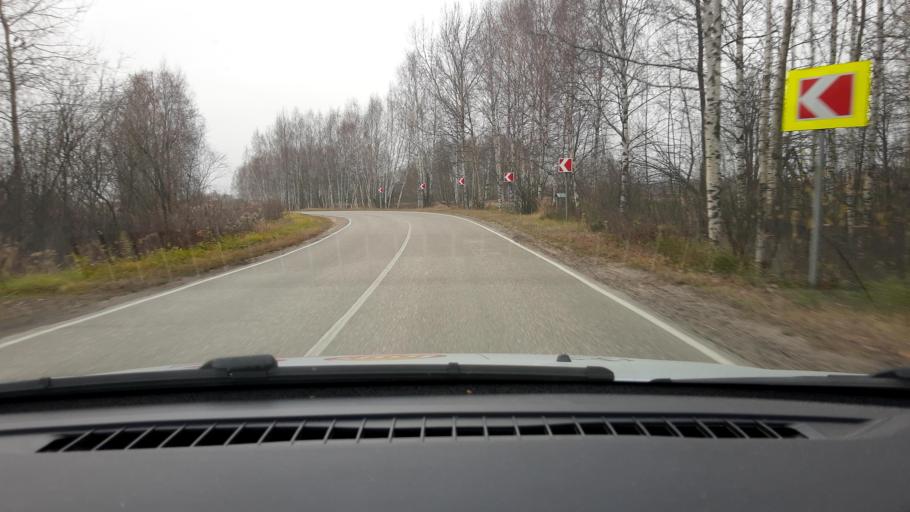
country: RU
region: Nizjnij Novgorod
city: Neklyudovo
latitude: 56.4641
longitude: 43.8995
